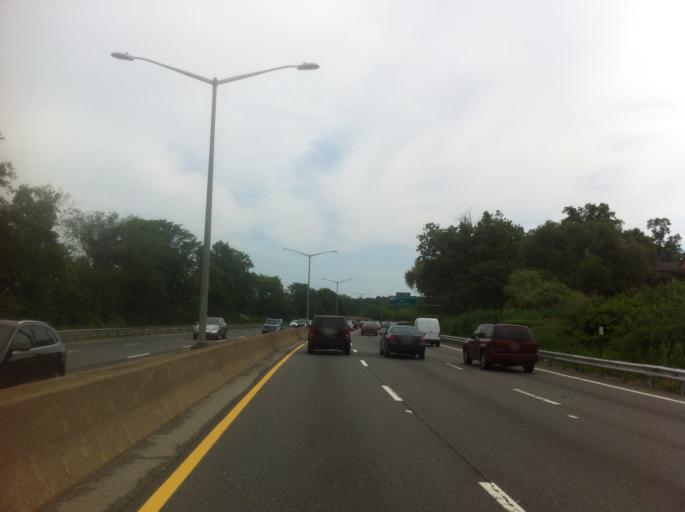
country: US
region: New York
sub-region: Nassau County
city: East Atlantic Beach
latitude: 40.7698
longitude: -73.7612
